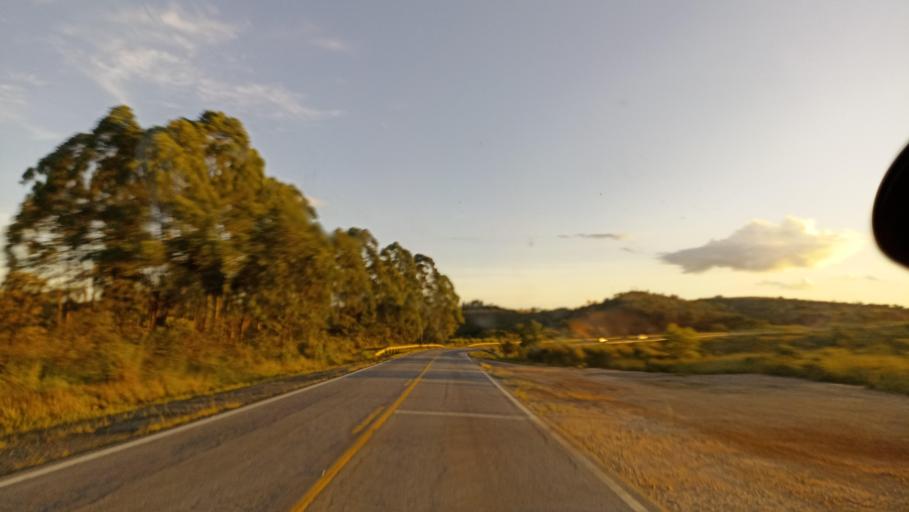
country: BR
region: Minas Gerais
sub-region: Sao Joao Del Rei
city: Sao Joao del Rei
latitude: -21.2222
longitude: -44.3607
